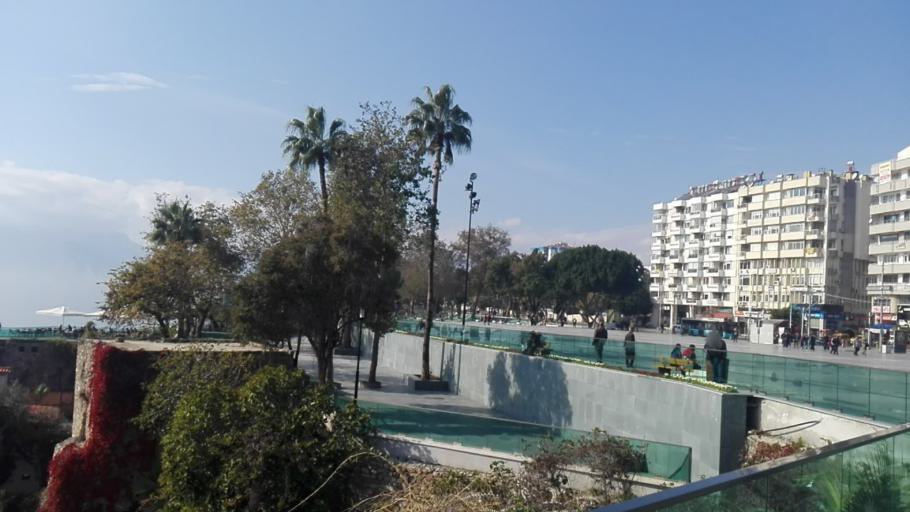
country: TR
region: Antalya
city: Antalya
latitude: 36.8866
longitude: 30.7035
